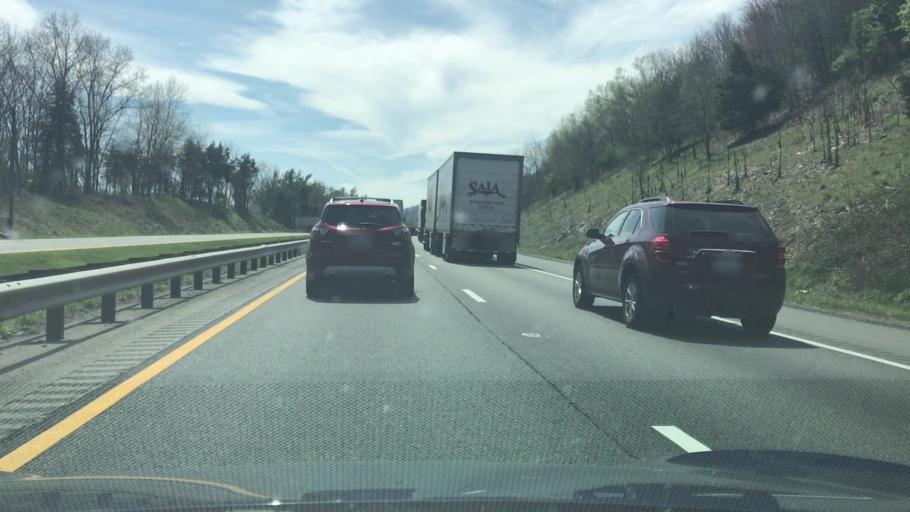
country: US
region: Virginia
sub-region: Pulaski County
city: Pulaski
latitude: 37.0436
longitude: -80.7177
